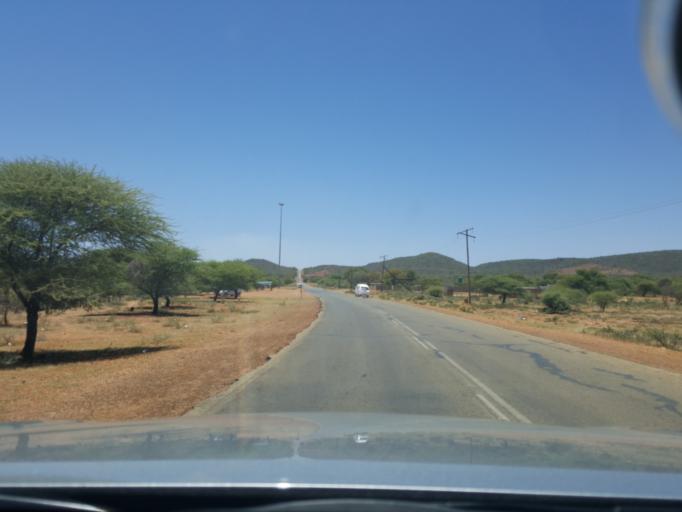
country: BW
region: South East
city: Lobatse
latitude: -25.2946
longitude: 25.9224
